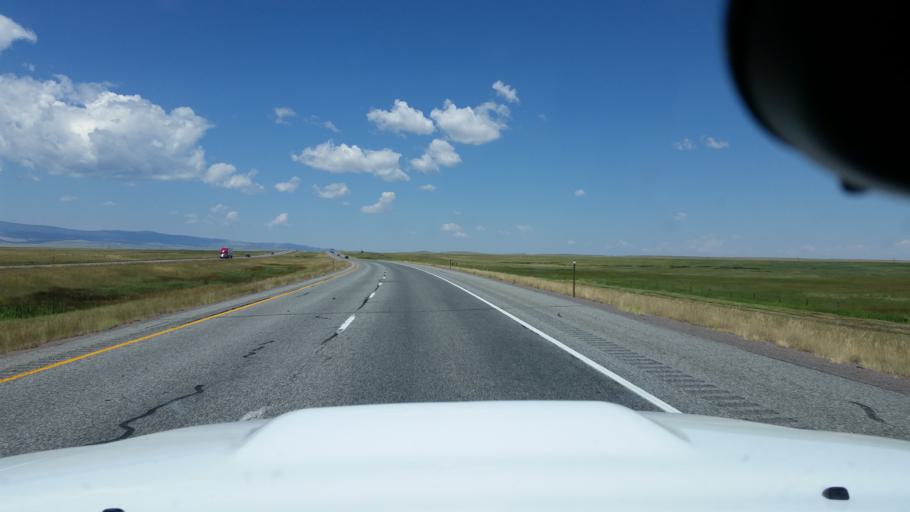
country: US
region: Wyoming
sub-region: Albany County
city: Laramie
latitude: 41.4112
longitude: -105.8393
